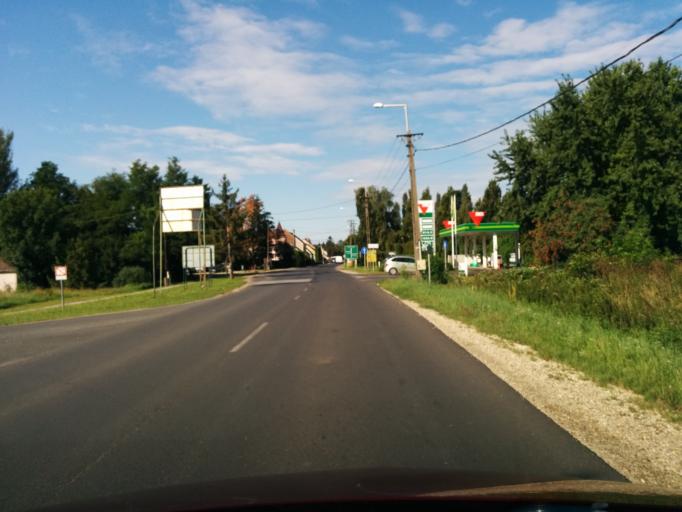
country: HU
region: Vas
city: Csepreg
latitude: 47.4055
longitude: 16.7182
